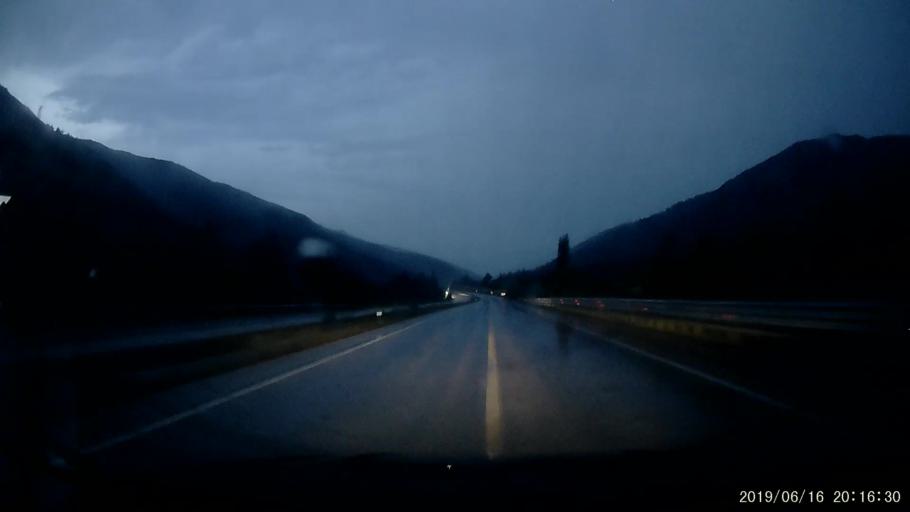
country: TR
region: Tokat
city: Resadiye
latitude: 40.3591
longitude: 37.4406
